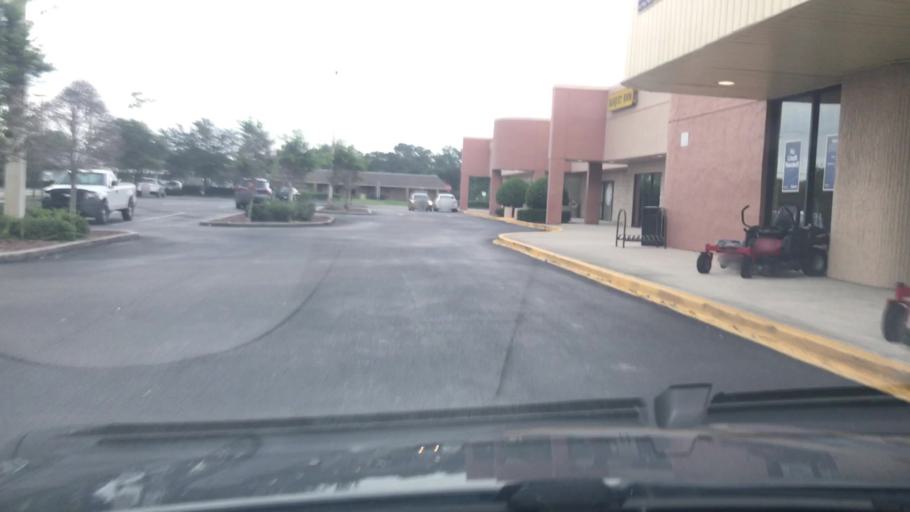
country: US
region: Florida
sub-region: Brevard County
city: Palm Bay
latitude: 28.0181
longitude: -80.6211
